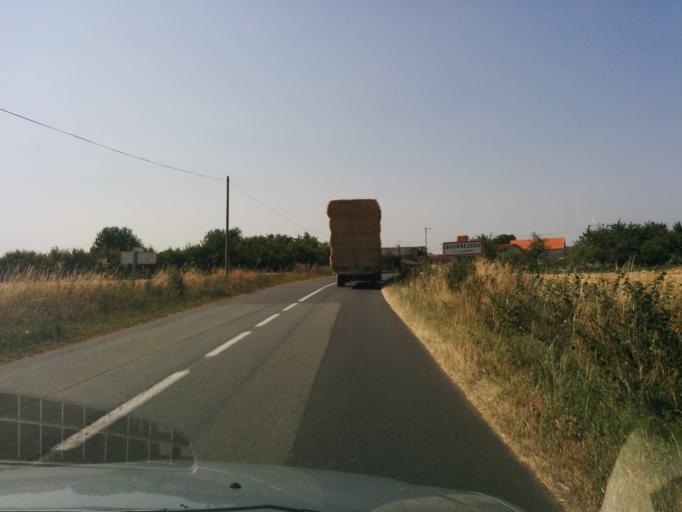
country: FR
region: Poitou-Charentes
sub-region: Departement de la Vienne
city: Mirebeau
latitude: 46.7439
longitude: 0.1789
